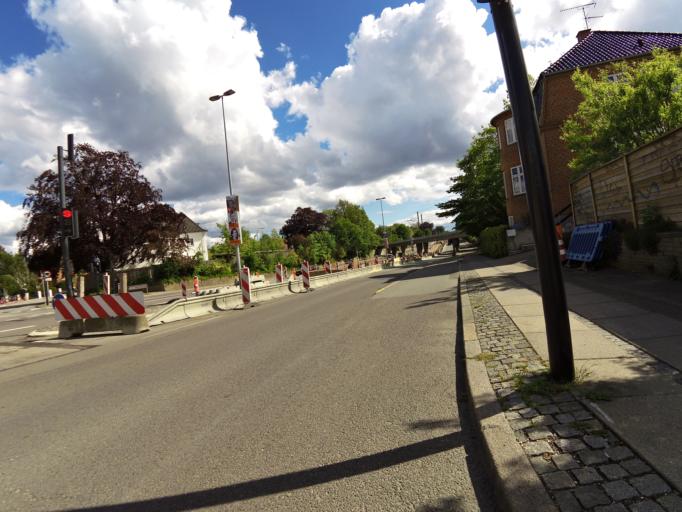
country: DK
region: Capital Region
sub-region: Gentofte Kommune
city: Charlottenlund
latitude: 55.7448
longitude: 12.5567
